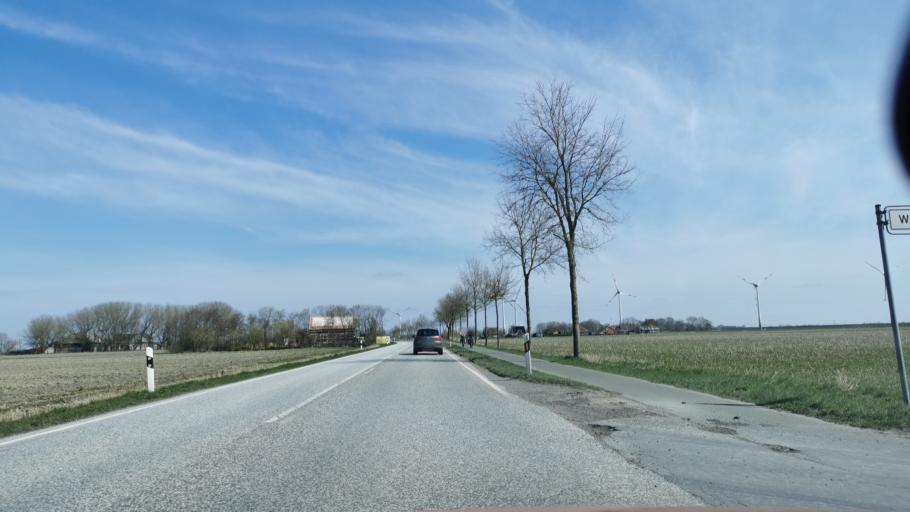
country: DE
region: Schleswig-Holstein
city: Wesselburener Deichhausen
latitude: 54.1537
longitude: 8.9344
